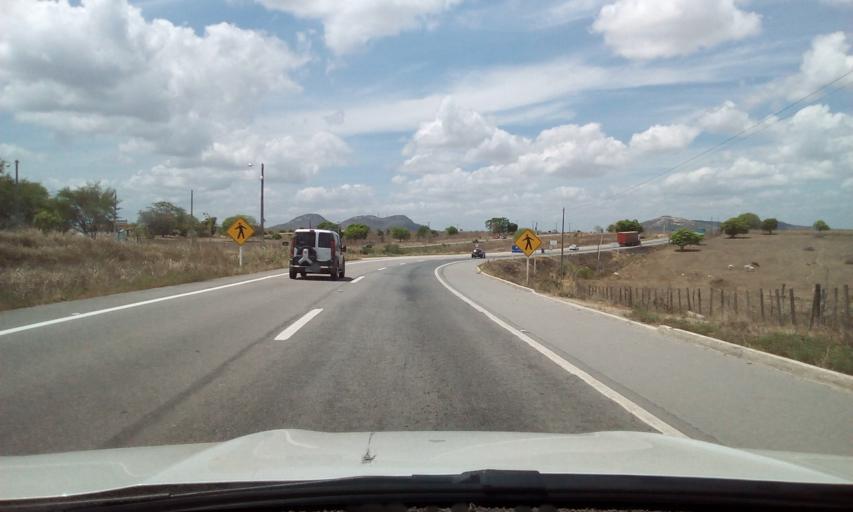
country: BR
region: Paraiba
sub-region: Gurinhem
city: Gurinhem
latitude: -7.1663
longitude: -35.3564
